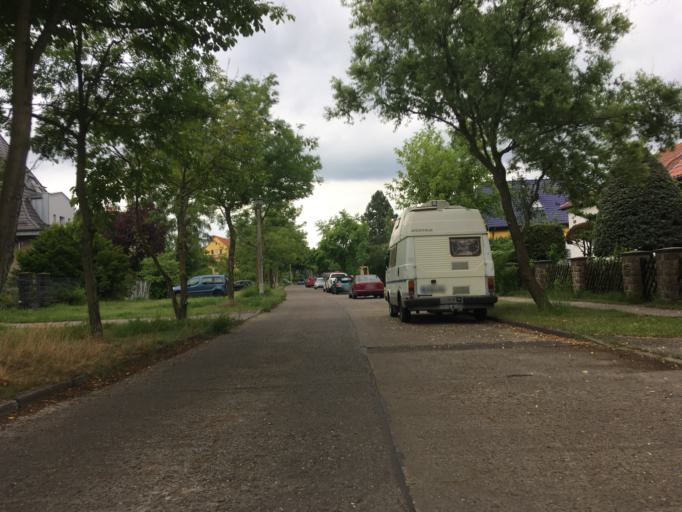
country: DE
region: Berlin
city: Friedrichshagen
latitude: 52.4504
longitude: 13.6400
